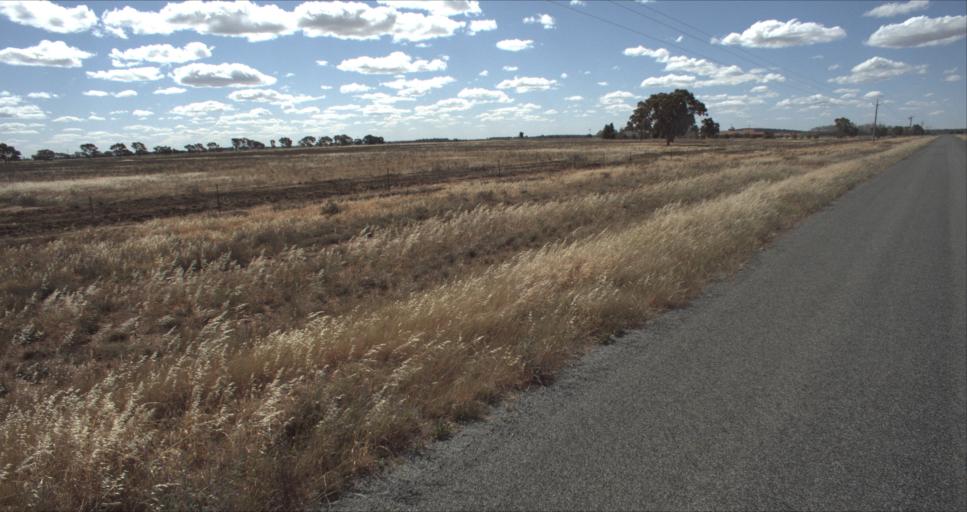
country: AU
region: New South Wales
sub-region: Leeton
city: Leeton
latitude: -34.4637
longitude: 146.2522
